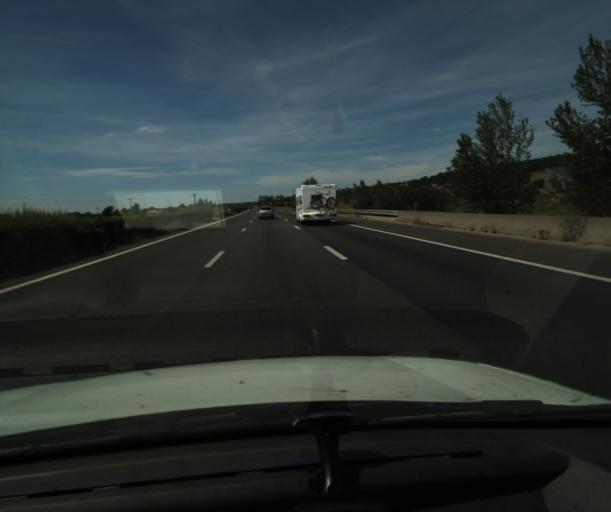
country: FR
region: Midi-Pyrenees
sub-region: Departement de la Haute-Garonne
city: Bruguieres
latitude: 43.7312
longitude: 1.3975
